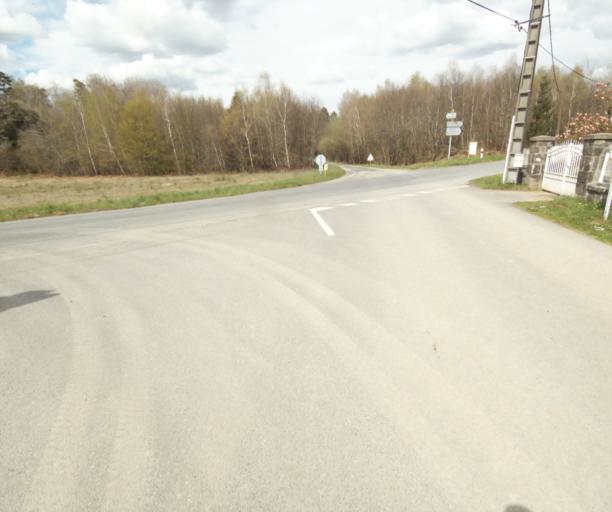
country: FR
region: Limousin
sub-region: Departement de la Correze
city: Argentat
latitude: 45.2035
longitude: 1.8935
